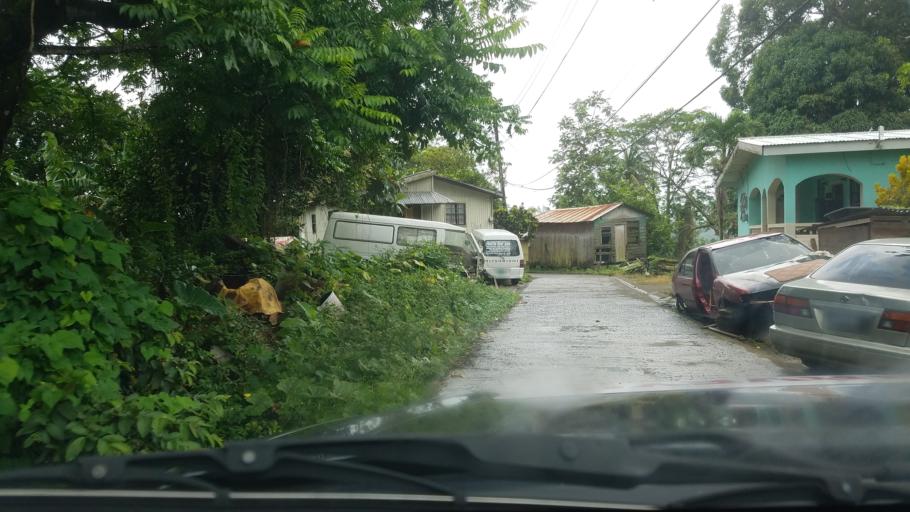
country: LC
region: Castries Quarter
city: Bisee
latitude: 13.9914
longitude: -60.9663
